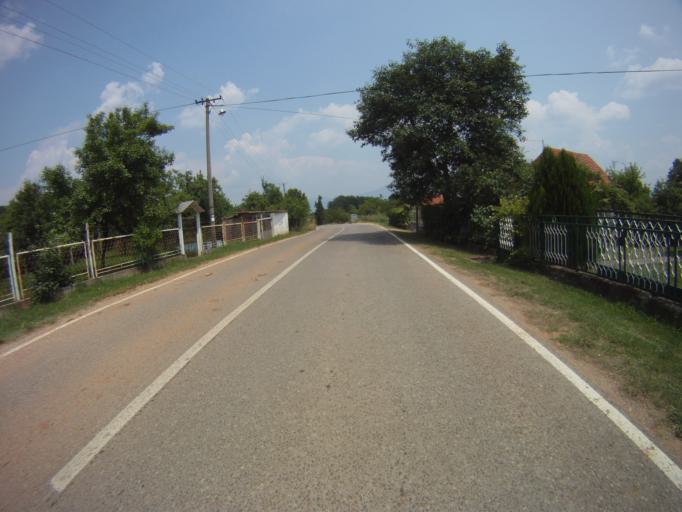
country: RS
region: Central Serbia
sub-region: Nisavski Okrug
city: Gadzin Han
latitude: 43.2029
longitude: 21.9687
